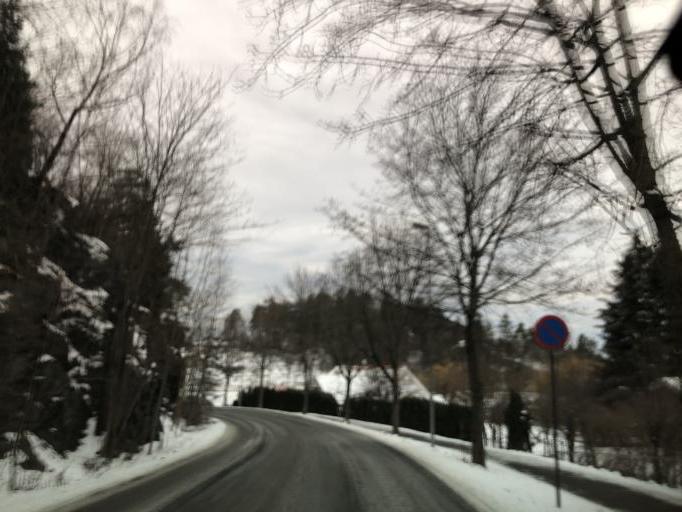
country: NO
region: Akershus
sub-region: Baerum
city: Sandvika
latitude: 59.8616
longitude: 10.5148
